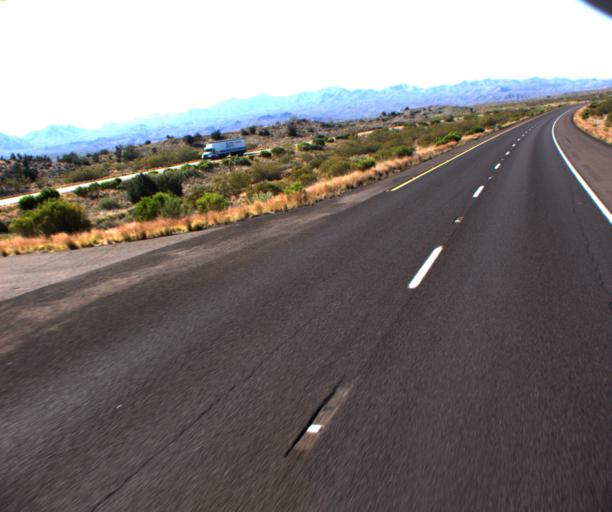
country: US
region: Arizona
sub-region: Mohave County
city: New Kingman-Butler
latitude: 35.1306
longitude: -113.6681
